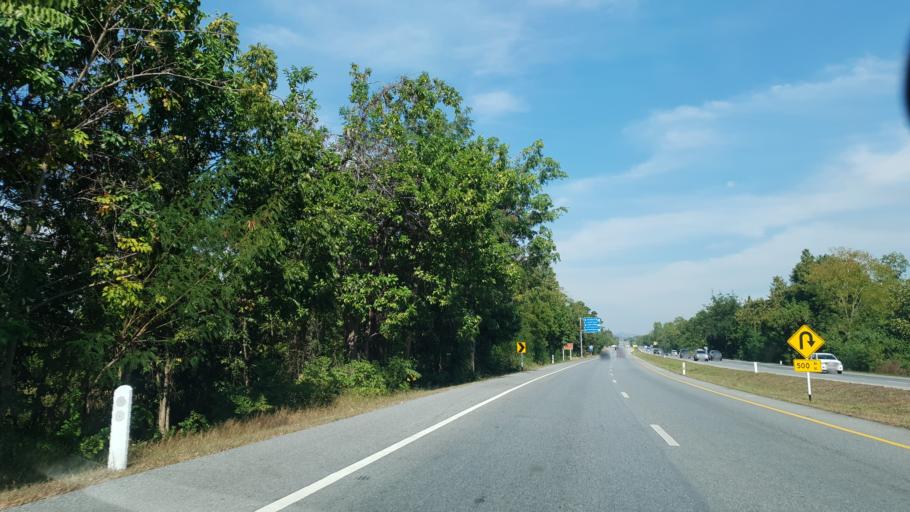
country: TH
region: Uttaradit
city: Thong Saen Khan
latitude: 17.4290
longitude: 100.2265
